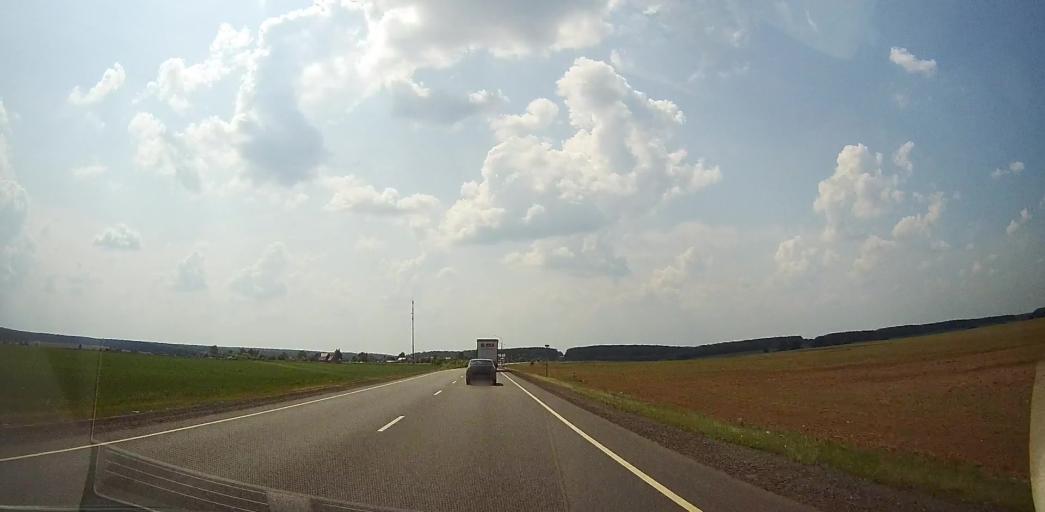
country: RU
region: Moskovskaya
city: Malino
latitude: 55.1295
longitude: 38.2482
